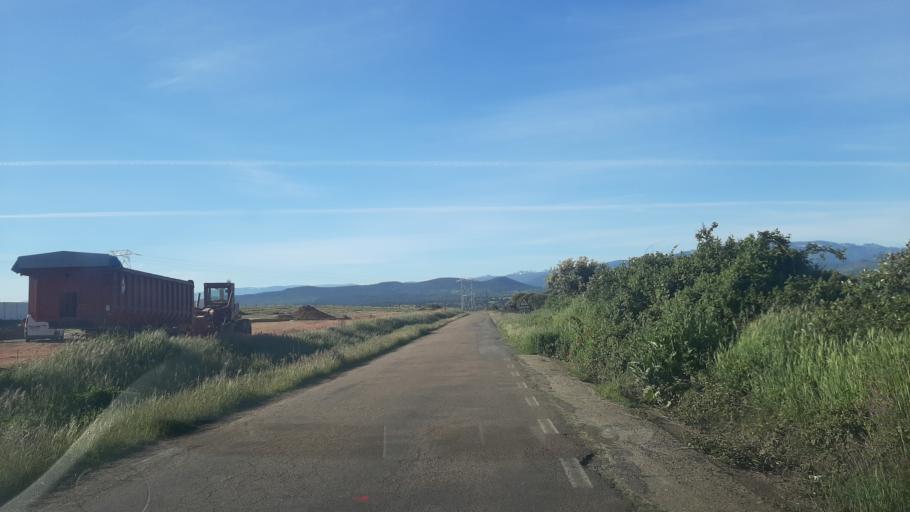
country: ES
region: Castille and Leon
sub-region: Provincia de Salamanca
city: Guijuelo
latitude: 40.5503
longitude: -5.6663
